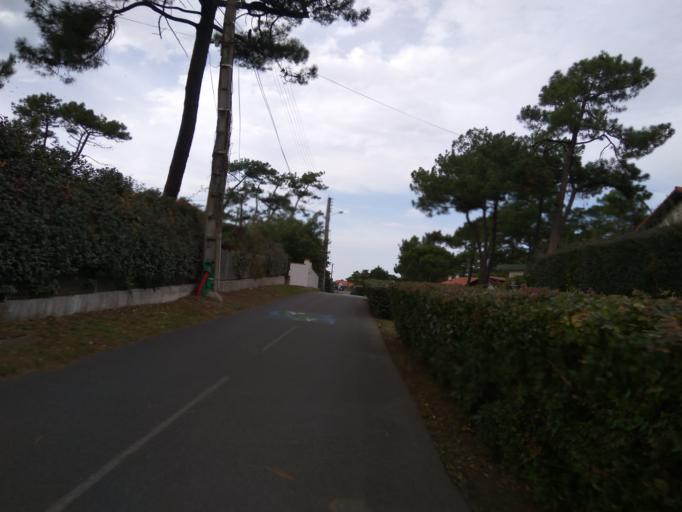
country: FR
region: Aquitaine
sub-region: Departement des Landes
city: Capbreton
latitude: 43.6402
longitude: -1.4402
